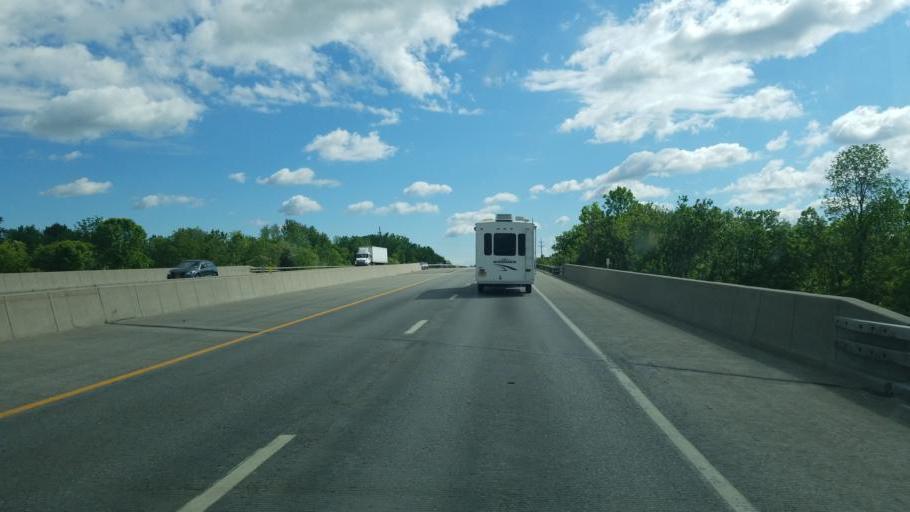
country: US
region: New York
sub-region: Cayuga County
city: Port Byron
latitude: 43.0409
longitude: -76.6281
